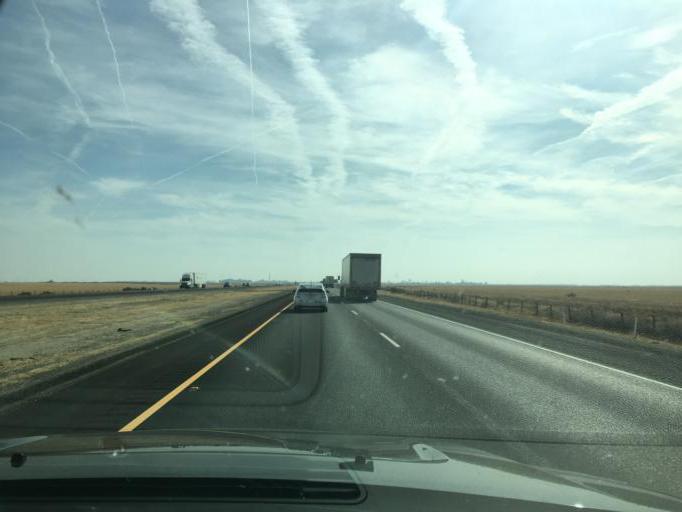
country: US
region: California
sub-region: Kern County
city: Lost Hills
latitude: 35.6369
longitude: -119.6688
